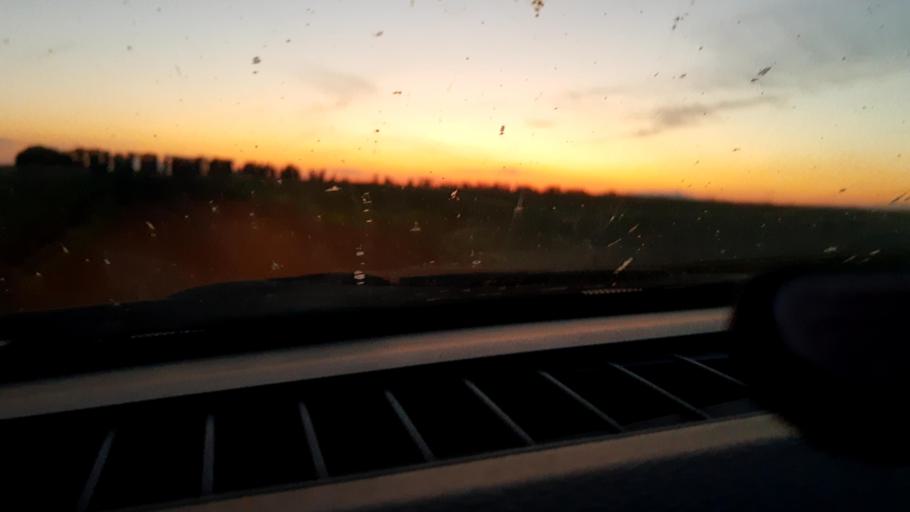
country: RU
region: Bashkortostan
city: Asanovo
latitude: 54.8618
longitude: 55.5864
